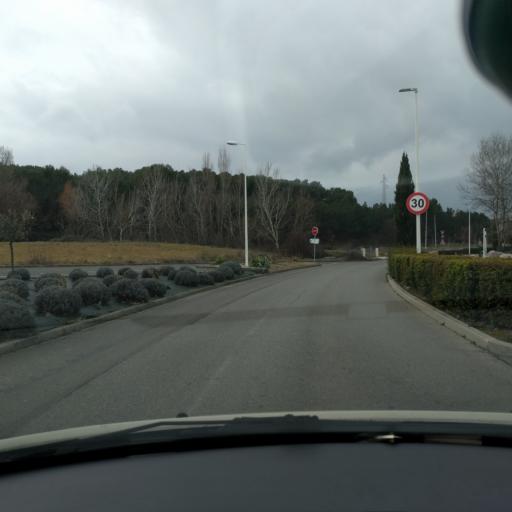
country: FR
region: Provence-Alpes-Cote d'Azur
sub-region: Departement des Bouches-du-Rhone
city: Bouc-Bel-Air
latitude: 43.4295
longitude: 5.4023
